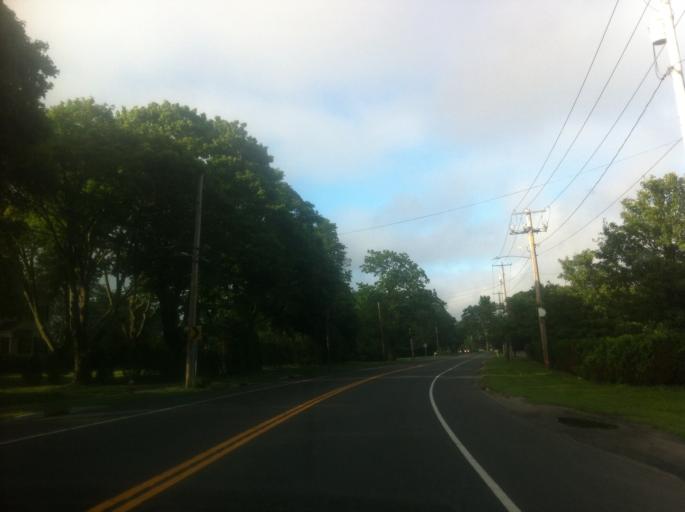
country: US
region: New York
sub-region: Suffolk County
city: Laurel
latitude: 40.9610
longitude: -72.5703
